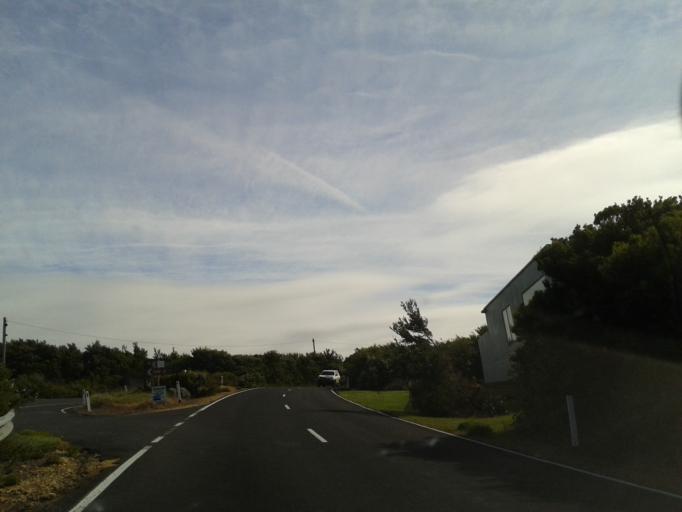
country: AU
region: Victoria
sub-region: Glenelg
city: Portland
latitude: -38.3702
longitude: 141.4051
